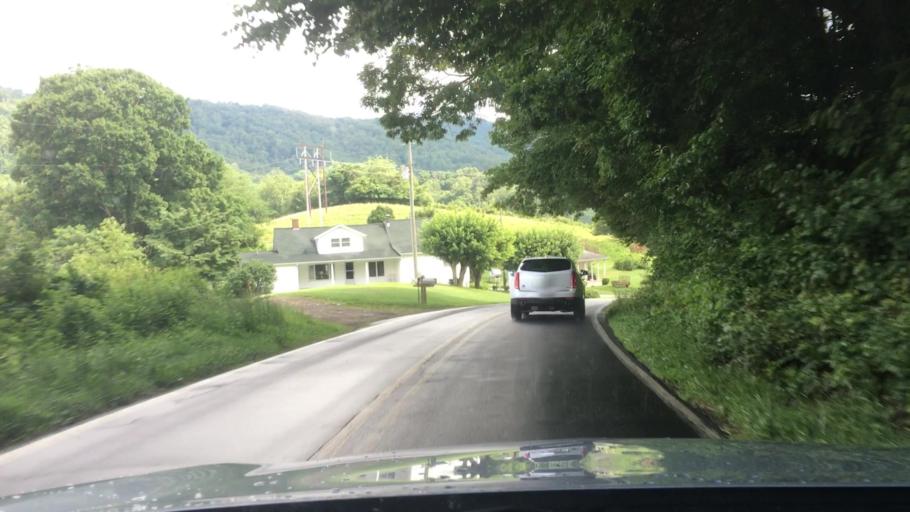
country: US
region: North Carolina
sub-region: Yancey County
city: Burnsville
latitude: 35.9054
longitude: -82.3588
